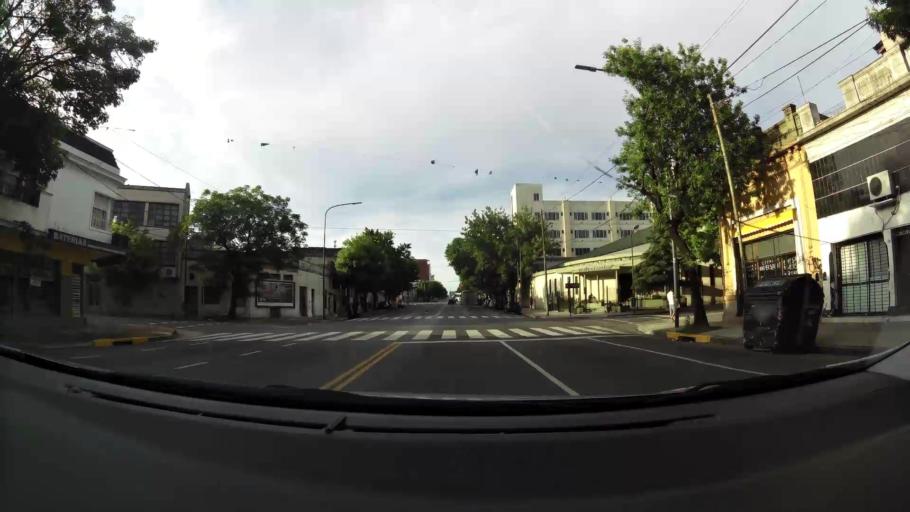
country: AR
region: Buenos Aires F.D.
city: Buenos Aires
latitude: -34.6414
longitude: -58.4232
